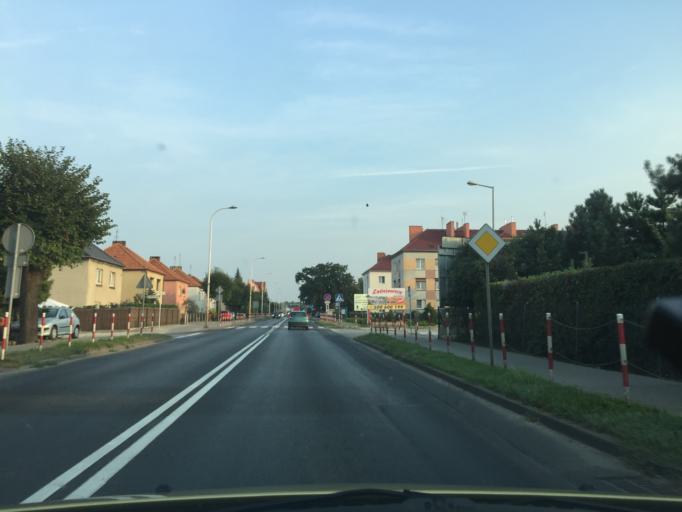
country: PL
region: Greater Poland Voivodeship
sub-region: Powiat jarocinski
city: Jarocin
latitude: 51.9654
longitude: 17.5082
